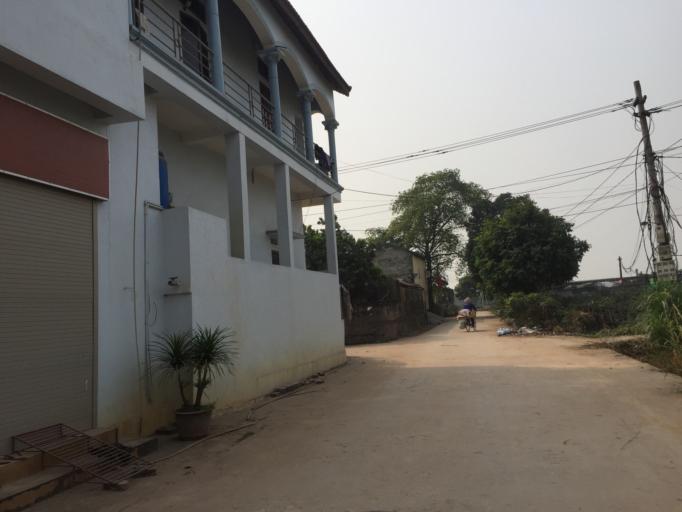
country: VN
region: Hung Yen
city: Van Giang
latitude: 20.9473
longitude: 105.9100
